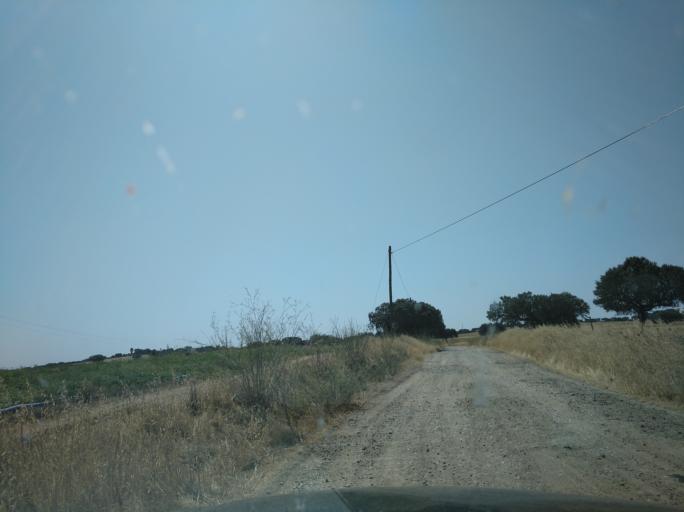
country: PT
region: Portalegre
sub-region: Campo Maior
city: Campo Maior
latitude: 39.0341
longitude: -6.9837
